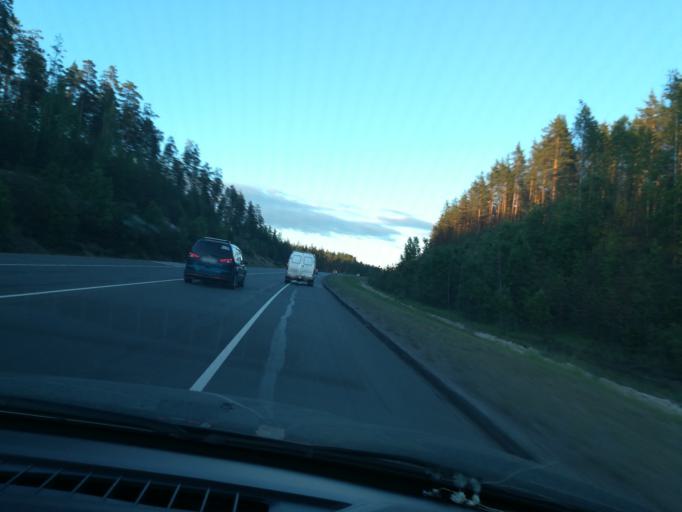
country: RU
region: Leningrad
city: Yakovlevo
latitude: 60.3625
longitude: 29.5578
